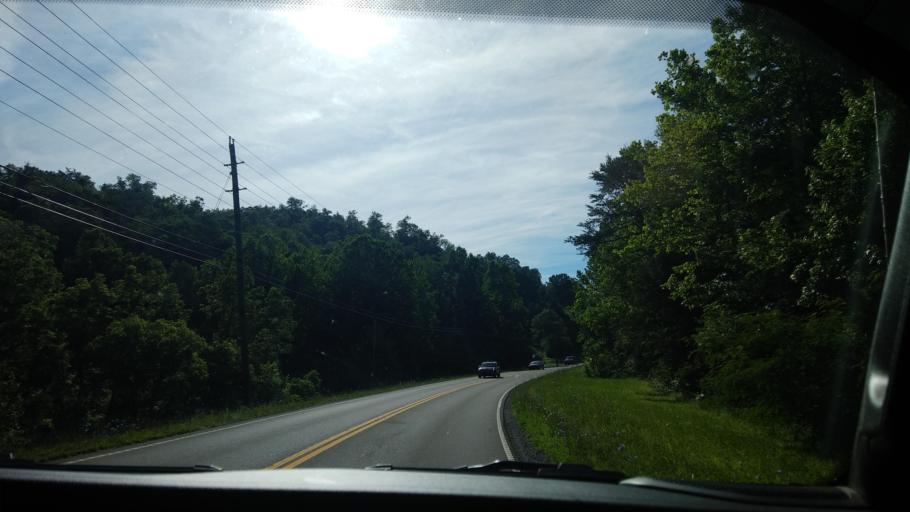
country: US
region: Tennessee
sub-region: Sevier County
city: Gatlinburg
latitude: 35.7616
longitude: -83.3731
